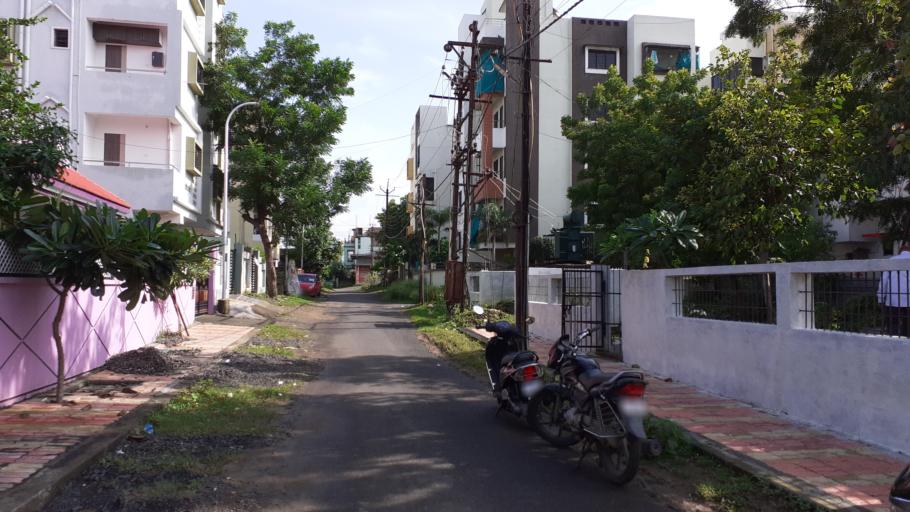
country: IN
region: Maharashtra
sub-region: Nagpur Division
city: Nagpur
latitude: 21.0978
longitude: 79.1091
